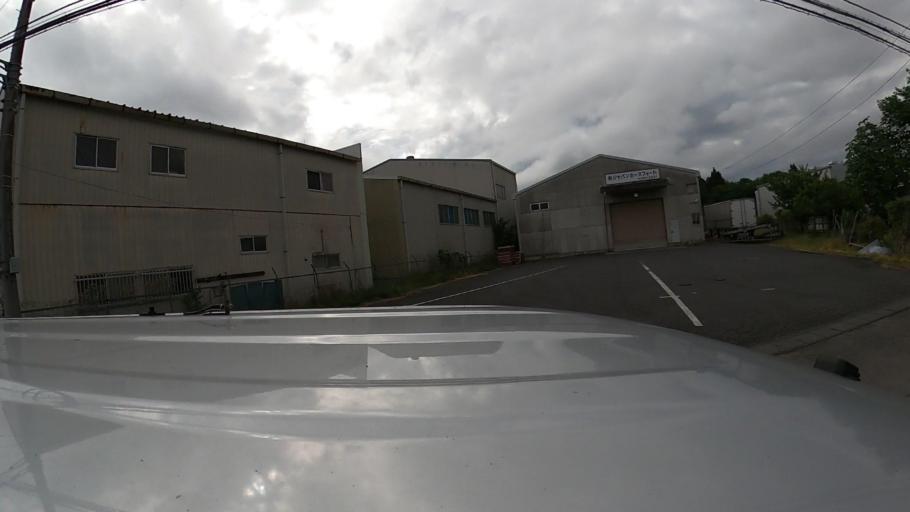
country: JP
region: Ibaraki
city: Inashiki
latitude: 36.0026
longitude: 140.2836
